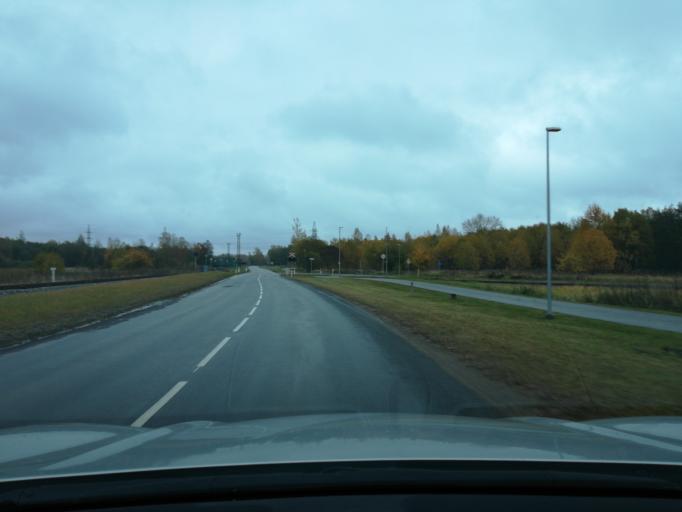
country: EE
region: Ida-Virumaa
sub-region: Johvi vald
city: Johvi
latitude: 59.3170
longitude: 27.4333
